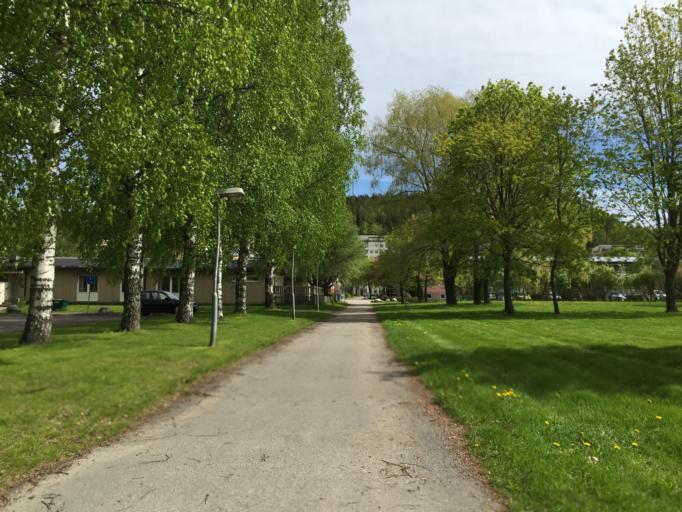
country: SE
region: Dalarna
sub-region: Ludvika Kommun
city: Ludvika
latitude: 60.1309
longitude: 15.1817
